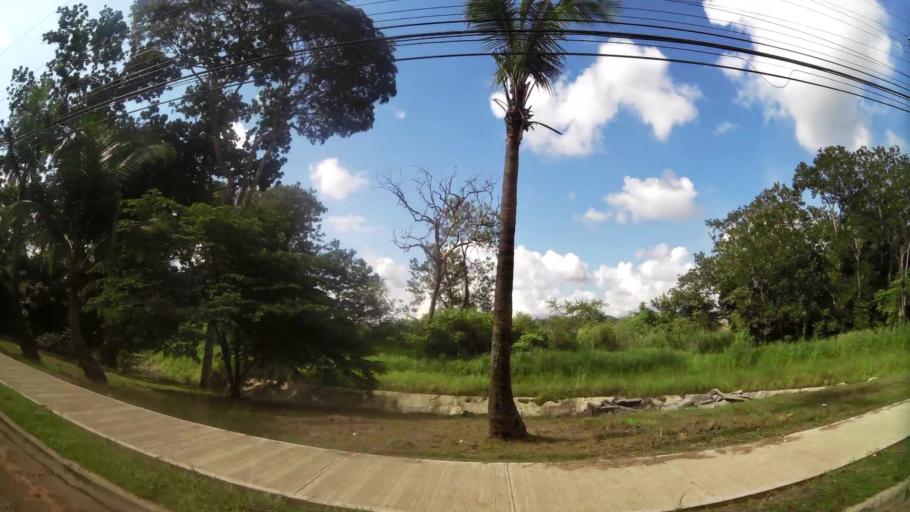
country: PA
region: Panama
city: Nuevo Arraijan
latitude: 8.9155
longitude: -79.7410
